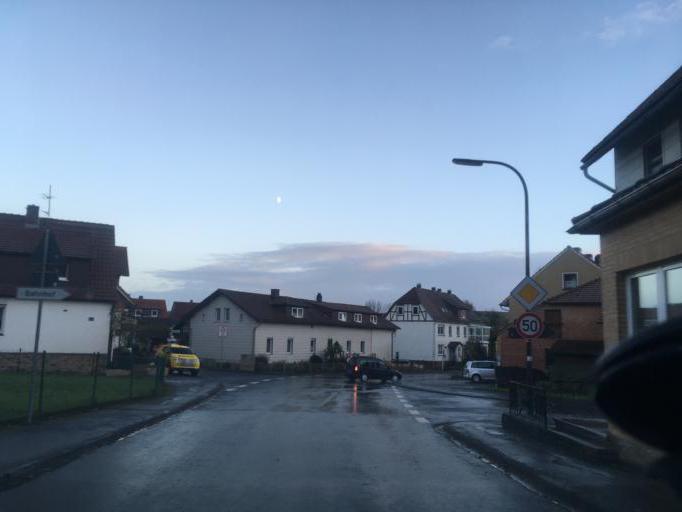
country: DE
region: Lower Saxony
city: Uslar
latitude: 51.6303
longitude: 9.6200
